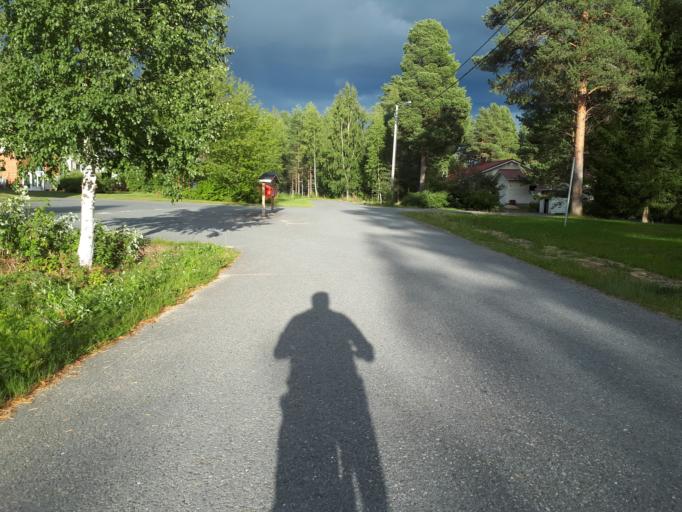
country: FI
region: Northern Ostrobothnia
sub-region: Oulunkaari
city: Ii
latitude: 65.3236
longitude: 25.4000
